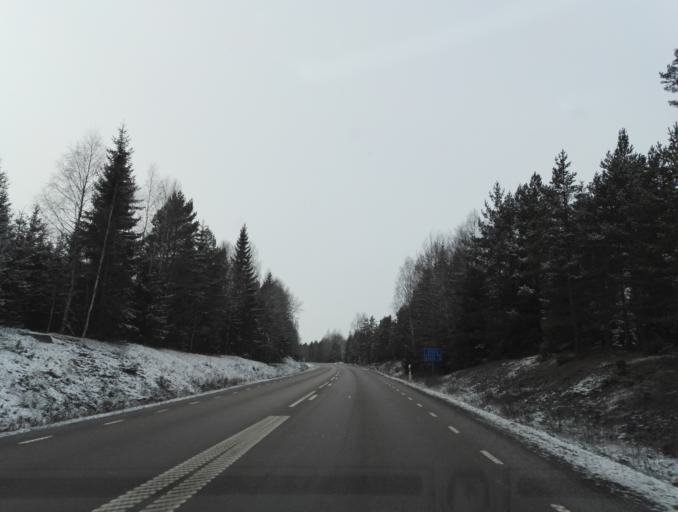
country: SE
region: Kronoberg
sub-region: Uppvidinge Kommun
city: Aseda
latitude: 57.1651
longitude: 15.4882
